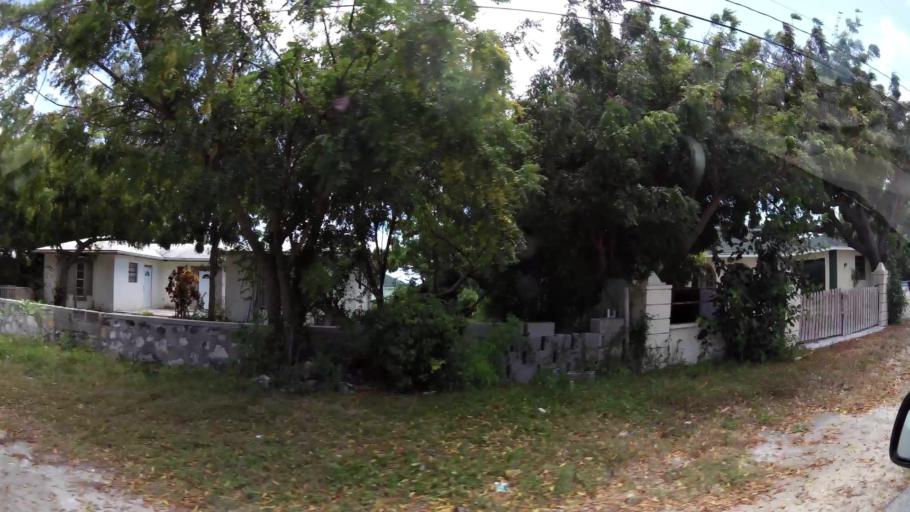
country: TC
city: Cockburn Town
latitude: 21.4556
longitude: -71.1417
